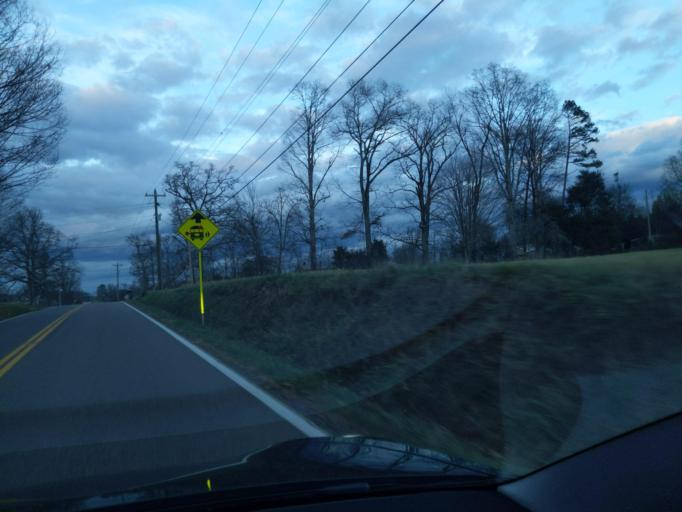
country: US
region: Tennessee
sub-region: Jefferson County
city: White Pine
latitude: 36.0891
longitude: -83.3636
